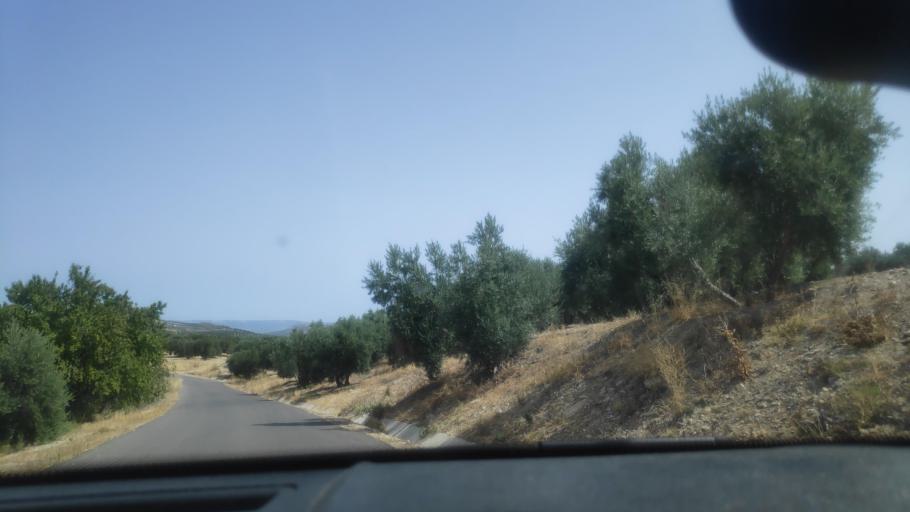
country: ES
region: Andalusia
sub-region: Provincia de Jaen
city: Jimena
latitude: 37.7965
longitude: -3.4482
